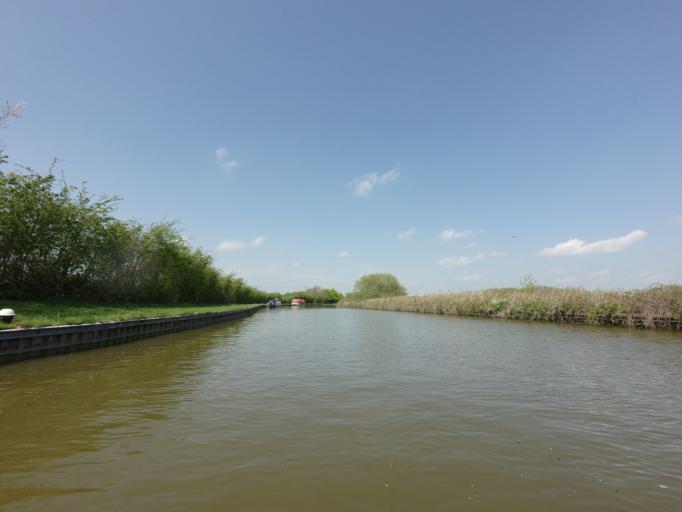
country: GB
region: England
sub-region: Buckinghamshire
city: Cheddington
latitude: 51.8560
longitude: -0.6459
